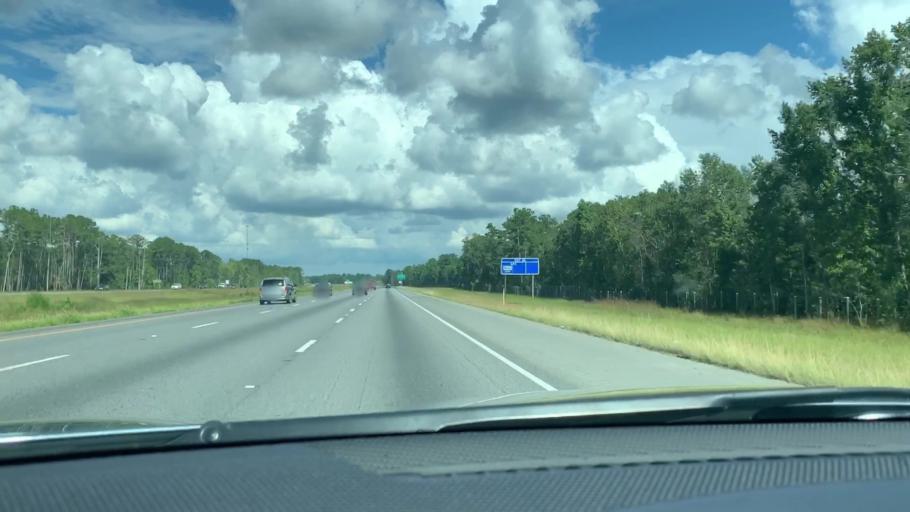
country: US
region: Georgia
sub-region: Glynn County
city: Brunswick
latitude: 31.0822
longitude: -81.6127
